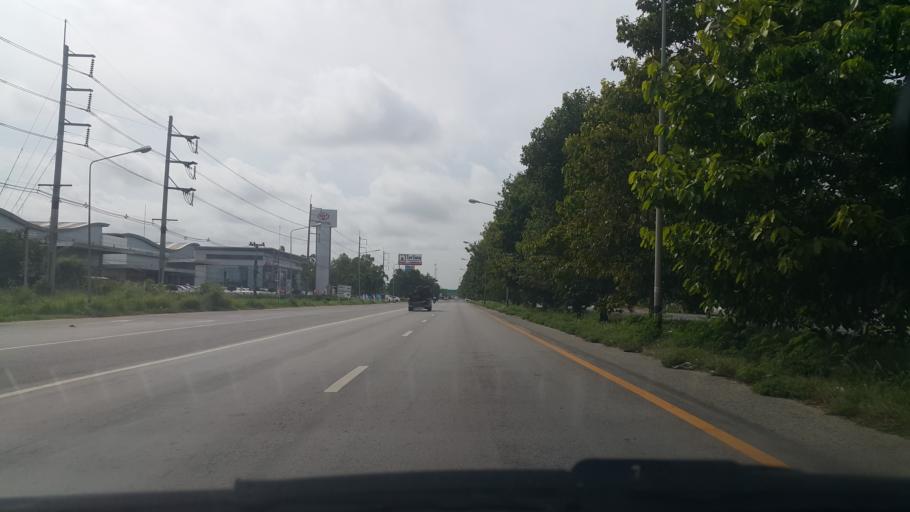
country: TH
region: Rayong
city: Rayong
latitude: 12.6654
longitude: 101.3083
